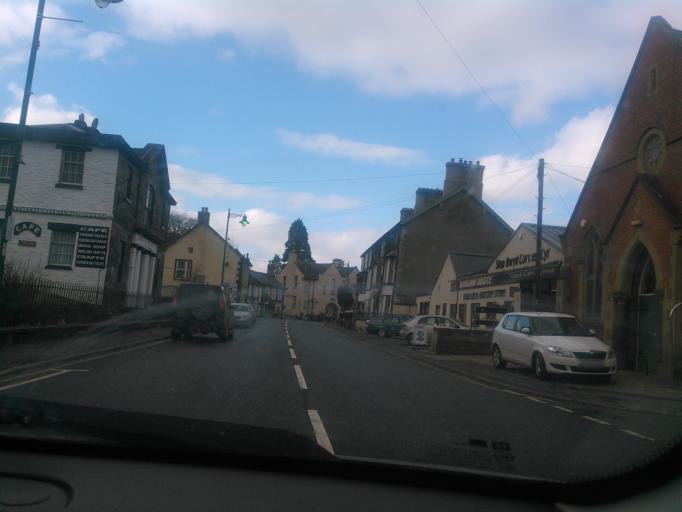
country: GB
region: Wales
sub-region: Denbighshire
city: Corwen
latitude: 52.9799
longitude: -3.3706
